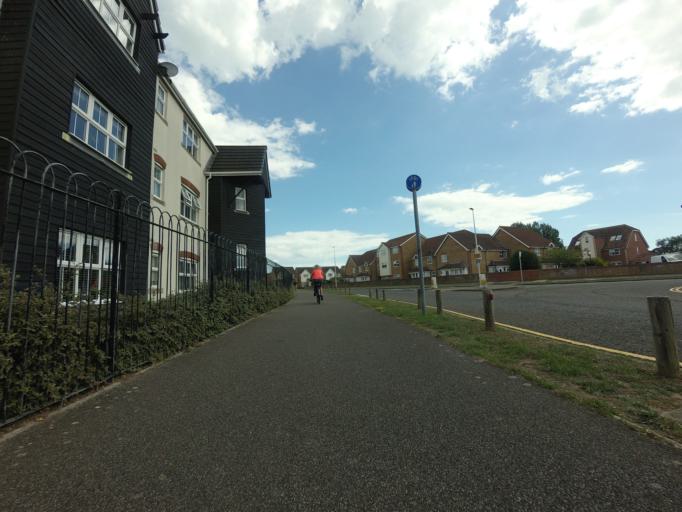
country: GB
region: England
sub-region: East Sussex
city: Pevensey
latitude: 50.7905
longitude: 0.3211
